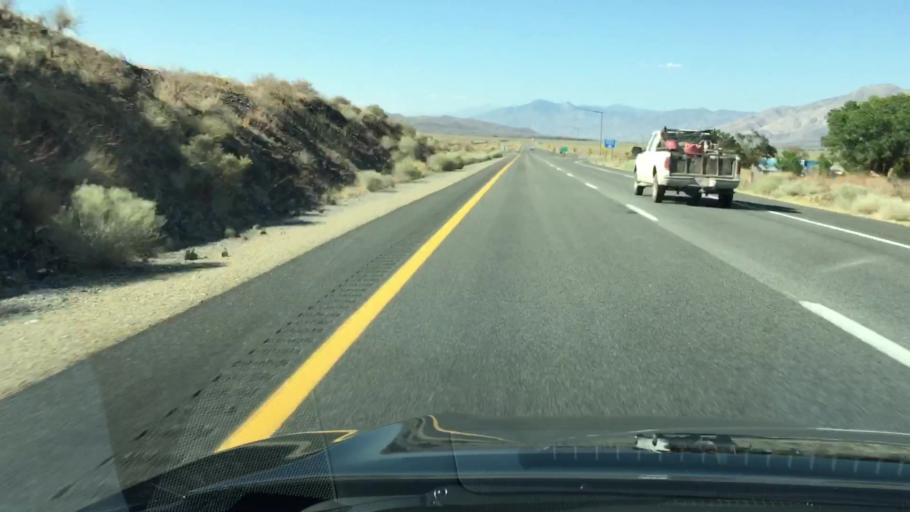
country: US
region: California
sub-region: Inyo County
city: Big Pine
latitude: 36.9442
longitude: -118.2403
